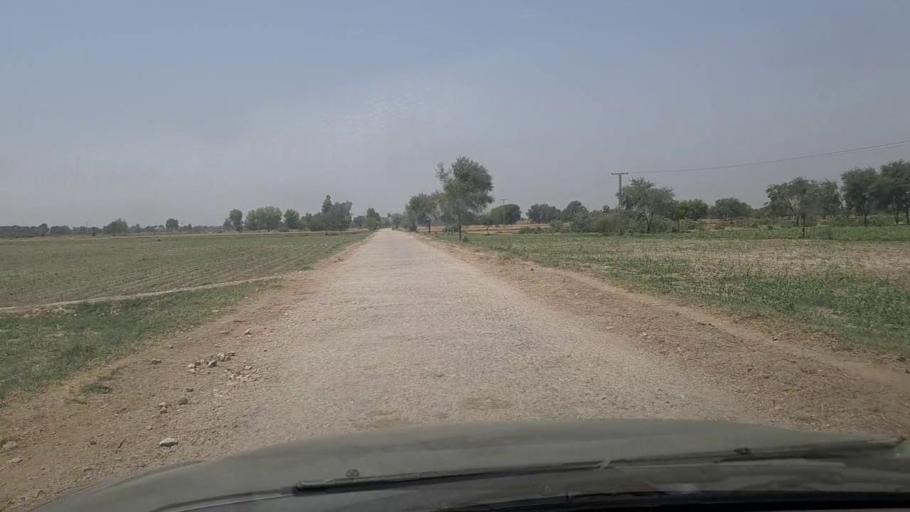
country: PK
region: Sindh
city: Adilpur
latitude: 27.9299
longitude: 69.2450
